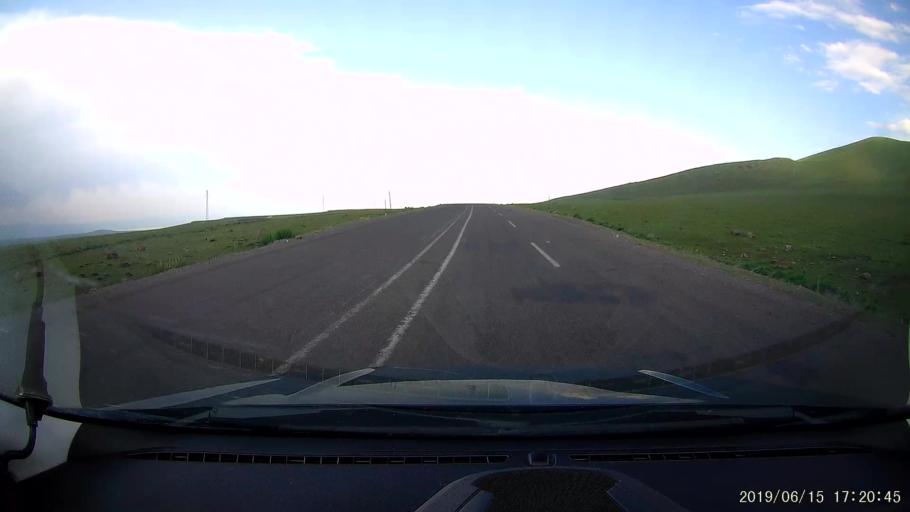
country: TR
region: Kars
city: Basgedikler
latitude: 40.6168
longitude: 43.3094
